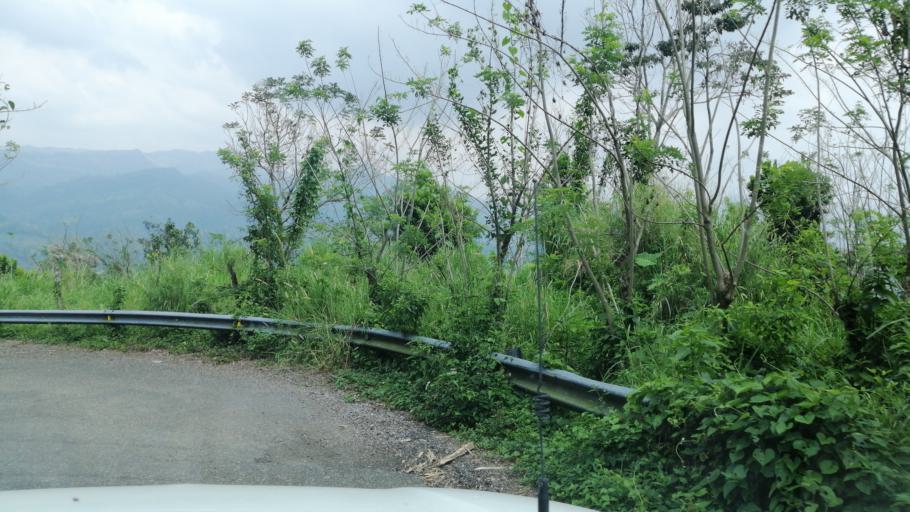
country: MX
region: Chiapas
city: Ostuacan
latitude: 17.3921
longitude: -93.3353
